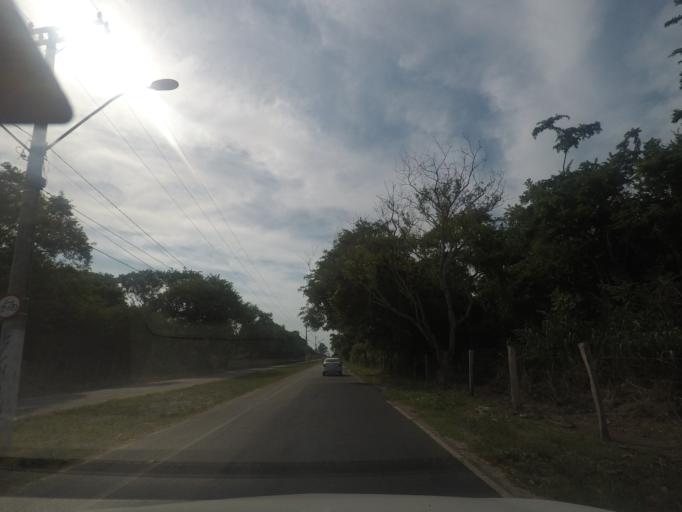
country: BR
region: Rio de Janeiro
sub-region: Marica
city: Marica
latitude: -22.9394
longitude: -42.8963
